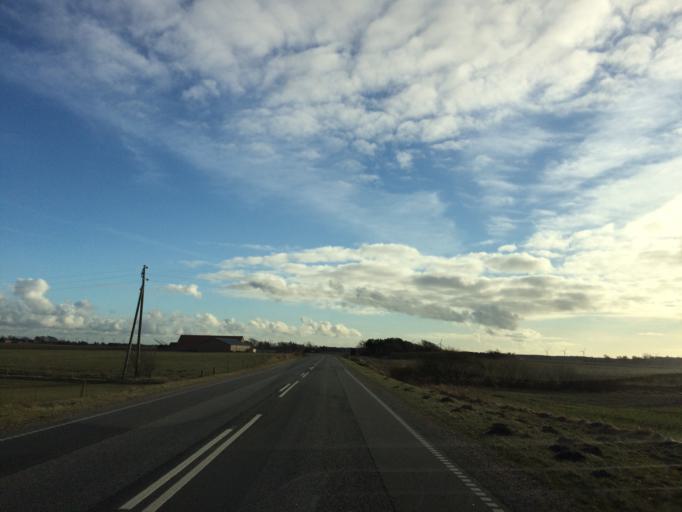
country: DK
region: Central Jutland
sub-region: Lemvig Kommune
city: Lemvig
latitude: 56.4377
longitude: 8.2969
